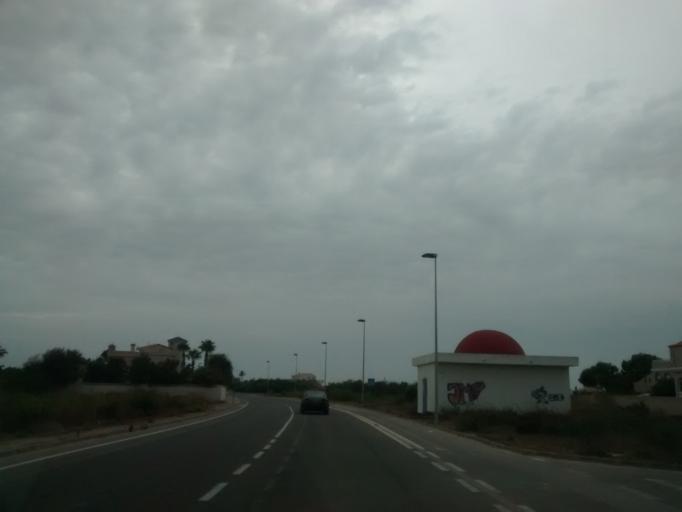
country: ES
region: Murcia
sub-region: Murcia
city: San Pedro del Pinatar
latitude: 37.7786
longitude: -0.7475
